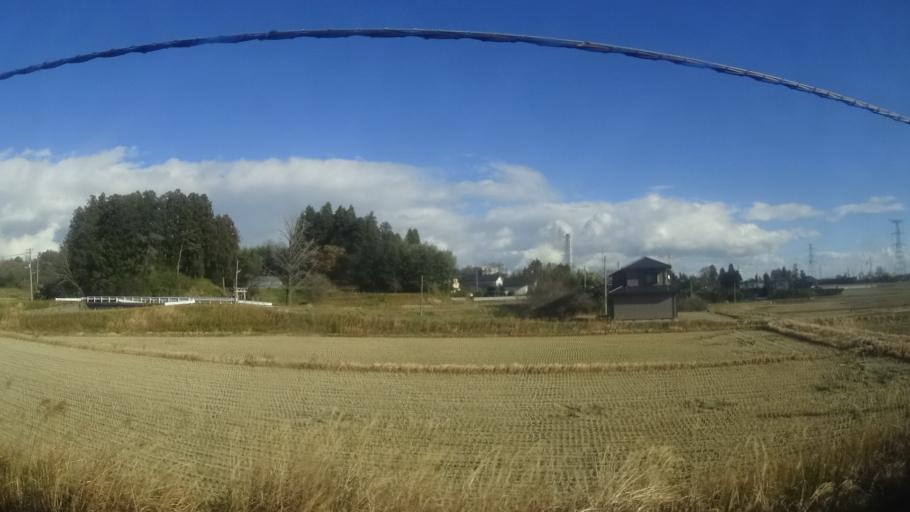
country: JP
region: Miyagi
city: Marumori
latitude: 37.8446
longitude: 140.9250
